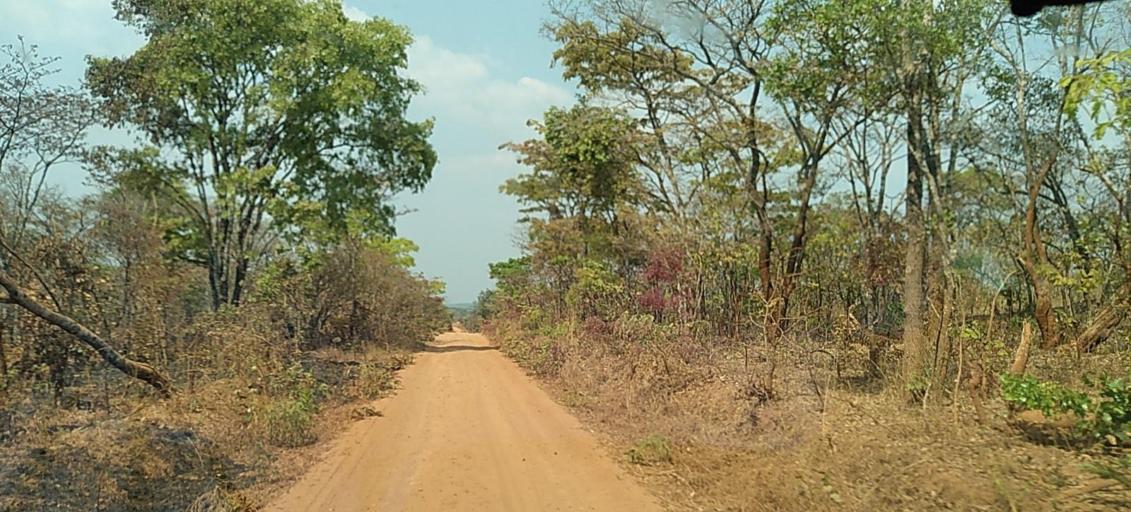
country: ZM
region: North-Western
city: Kasempa
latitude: -13.3064
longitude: 26.0713
